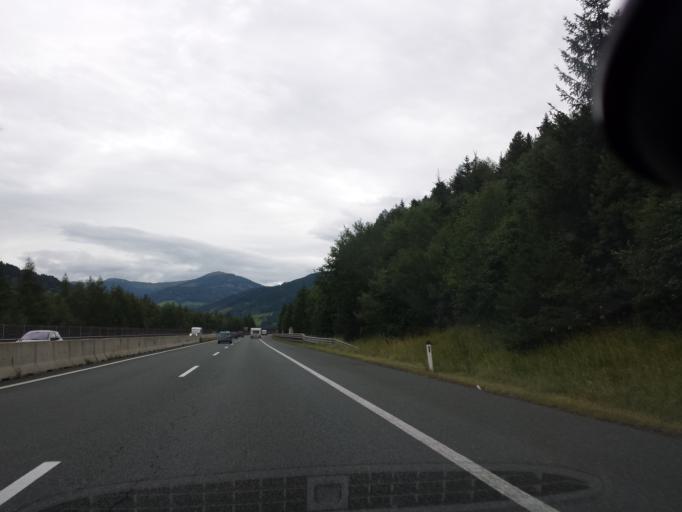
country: AT
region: Carinthia
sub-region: Politischer Bezirk Spittal an der Drau
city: Gmuend
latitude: 46.9239
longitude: 13.5850
